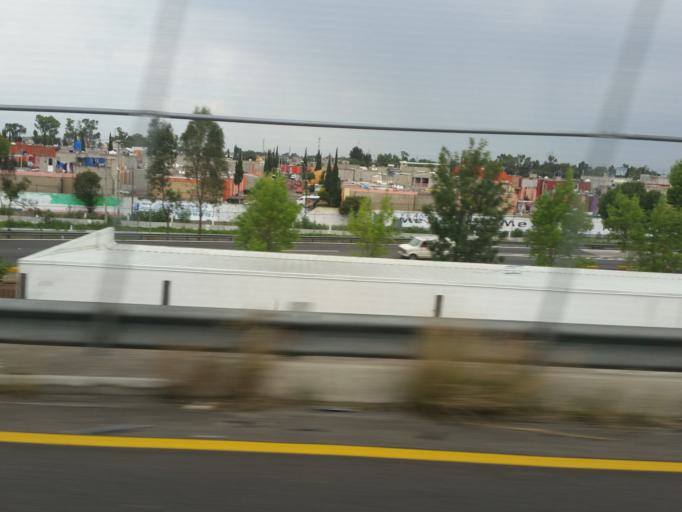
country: MX
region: Mexico
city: Ecatepec
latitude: 19.6098
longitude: -99.0341
